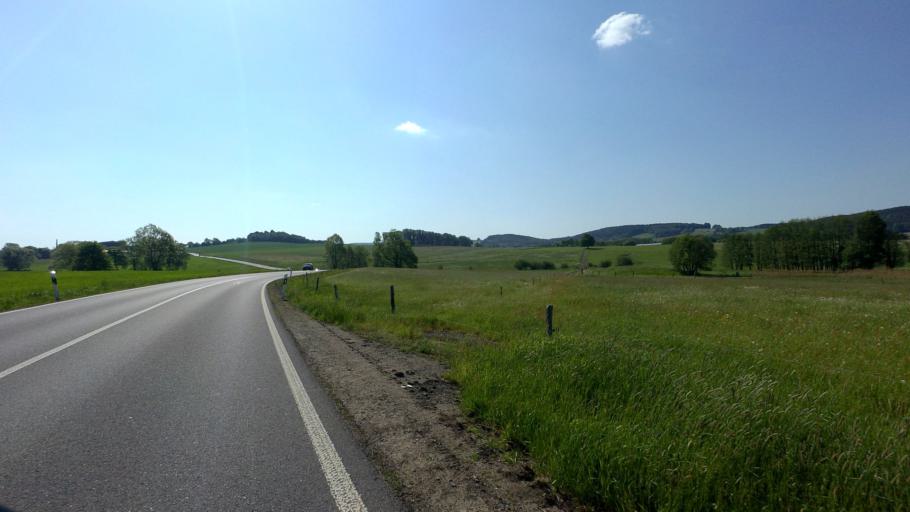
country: DE
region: Saxony
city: Neustadt in Sachsen
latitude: 51.0352
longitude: 14.1706
